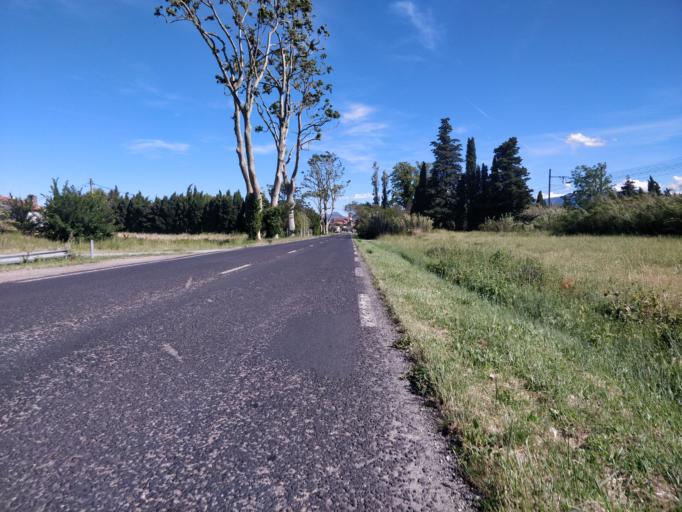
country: FR
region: Languedoc-Roussillon
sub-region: Departement des Pyrenees-Orientales
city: Elne
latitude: 42.6098
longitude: 2.9621
